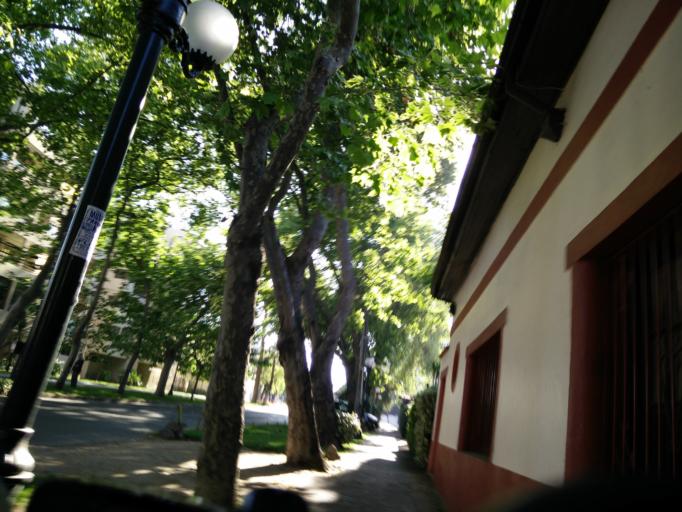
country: CL
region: Santiago Metropolitan
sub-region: Provincia de Santiago
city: Villa Presidente Frei, Nunoa, Santiago, Chile
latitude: -33.4438
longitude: -70.6055
